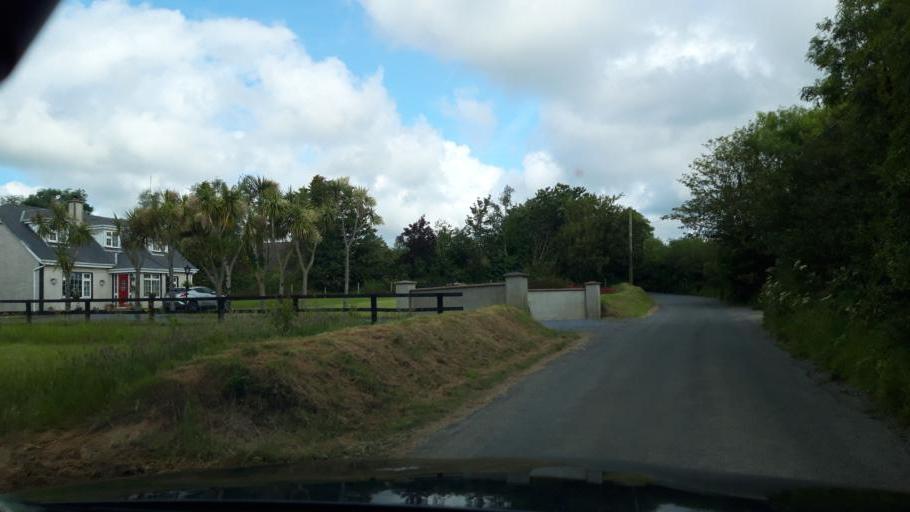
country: IE
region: Leinster
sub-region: Loch Garman
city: Loch Garman
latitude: 52.2817
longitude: -6.4951
